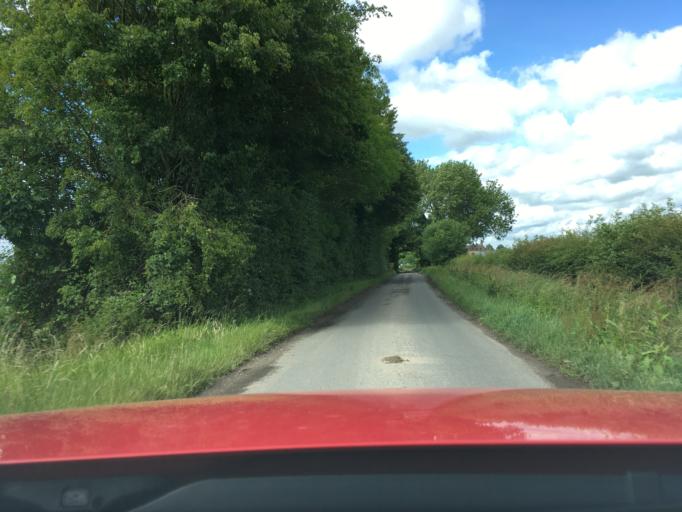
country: GB
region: England
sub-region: Gloucestershire
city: Gloucester
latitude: 51.8440
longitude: -2.3408
